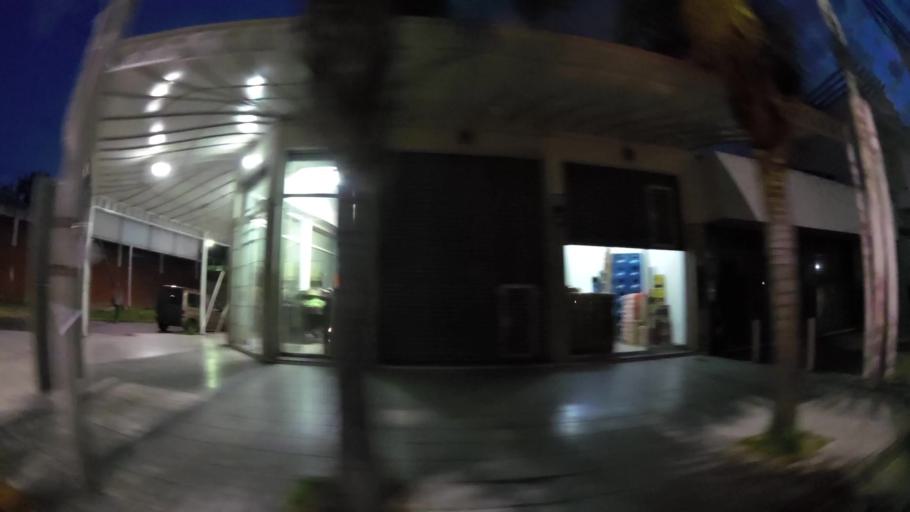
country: AR
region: Buenos Aires
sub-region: Partido de Quilmes
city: Quilmes
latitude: -34.6993
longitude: -58.3081
